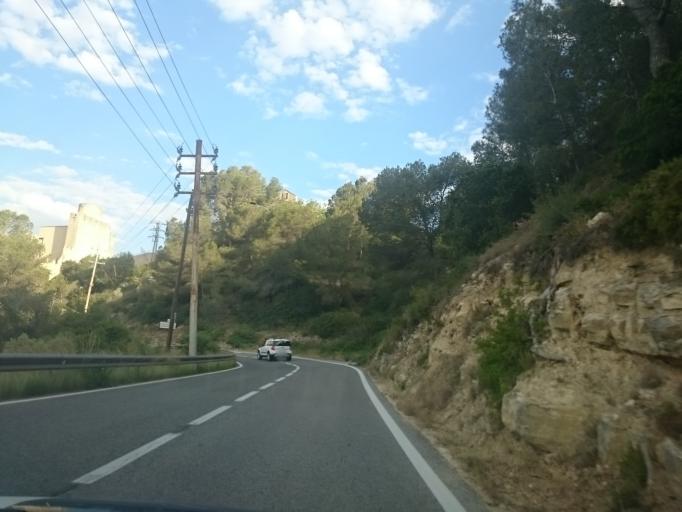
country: ES
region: Catalonia
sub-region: Provincia de Barcelona
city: Castellet
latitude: 41.2642
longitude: 1.6384
